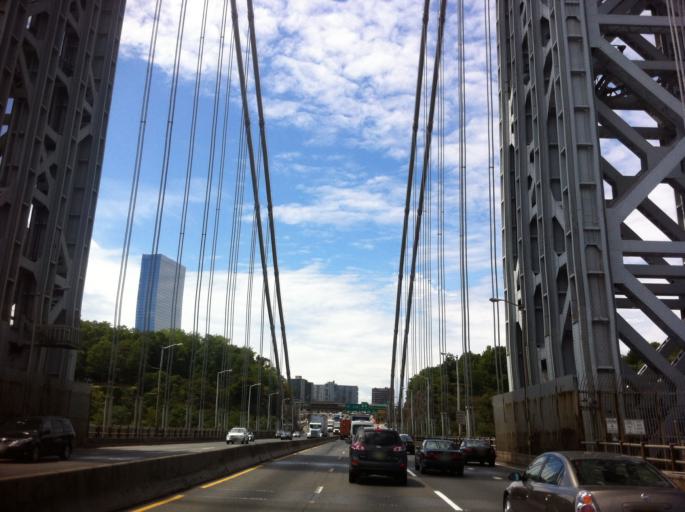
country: US
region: New Jersey
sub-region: Bergen County
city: Fort Lee
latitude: 40.8528
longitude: -73.9584
